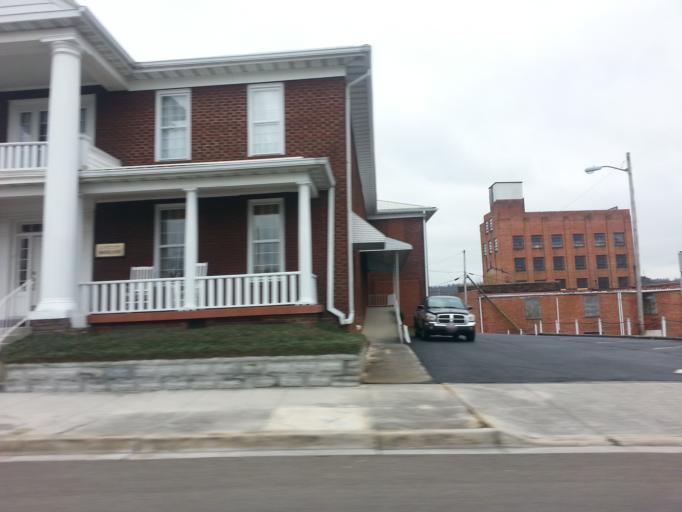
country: US
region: Tennessee
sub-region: Hamblen County
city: Morristown
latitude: 36.2143
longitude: -83.2916
